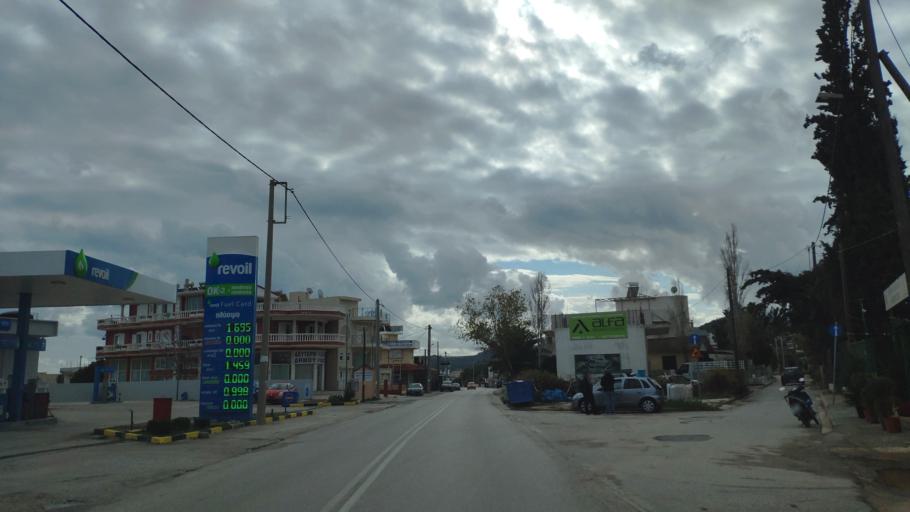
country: GR
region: Attica
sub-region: Nomarchia Anatolikis Attikis
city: Artemida
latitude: 37.9446
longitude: 24.0078
